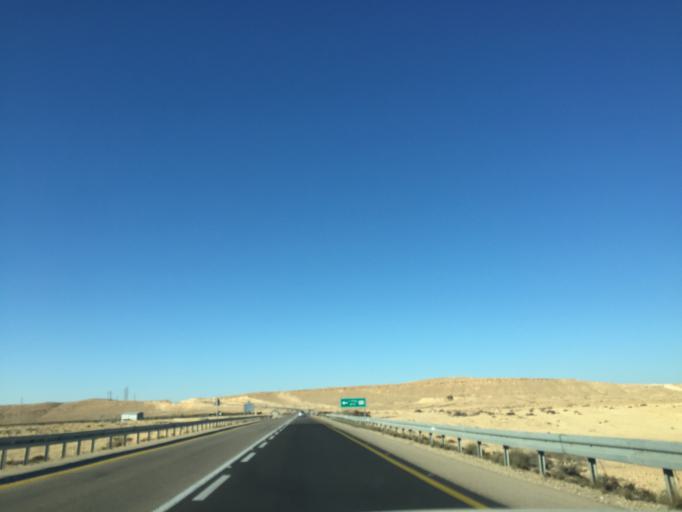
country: IL
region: Southern District
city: Mitzpe Ramon
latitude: 30.6568
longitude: 34.8109
